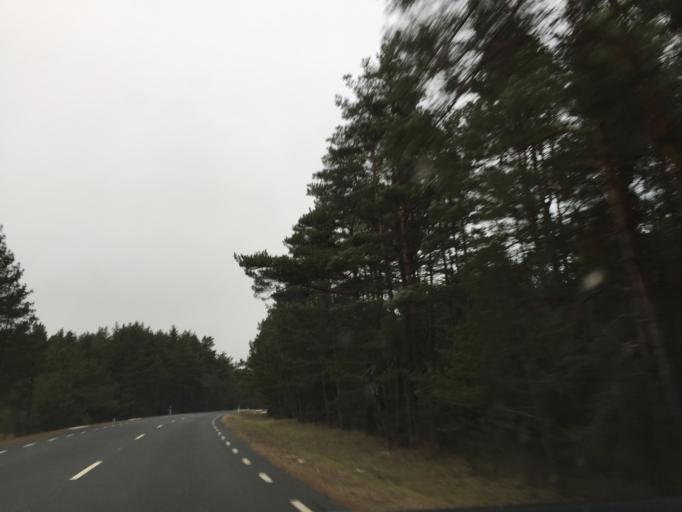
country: EE
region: Saare
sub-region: Kuressaare linn
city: Kuressaare
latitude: 58.5554
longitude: 22.3165
